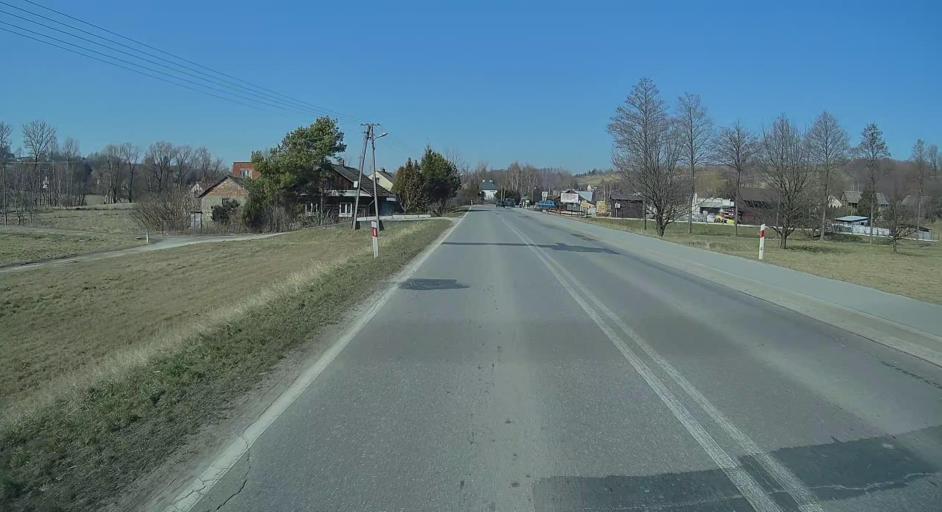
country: PL
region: Subcarpathian Voivodeship
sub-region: Powiat rzeszowski
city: Chmielnik
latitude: 49.9578
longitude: 22.0984
